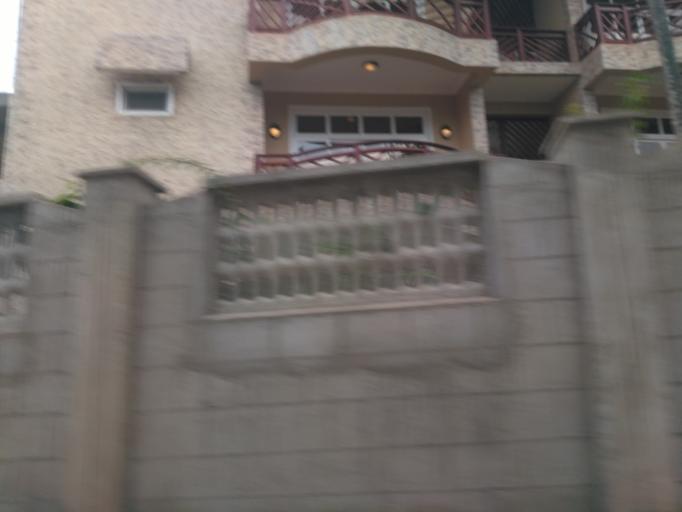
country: TZ
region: Dar es Salaam
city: Dar es Salaam
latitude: -6.8518
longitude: 39.3586
